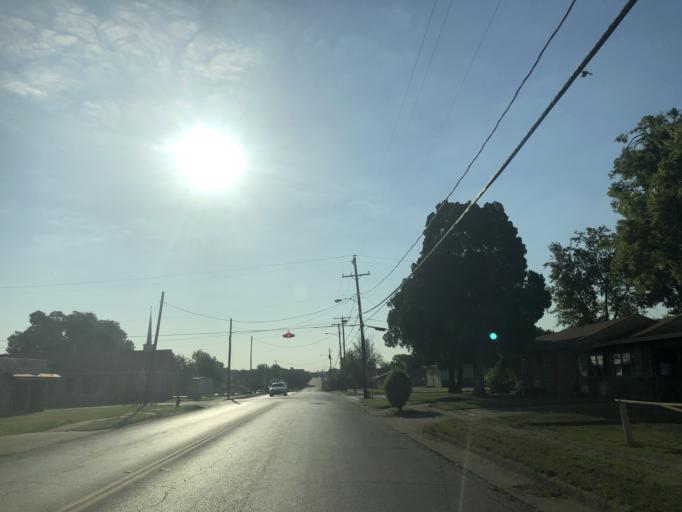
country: US
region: Texas
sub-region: Dallas County
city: Grand Prairie
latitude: 32.7350
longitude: -97.0298
